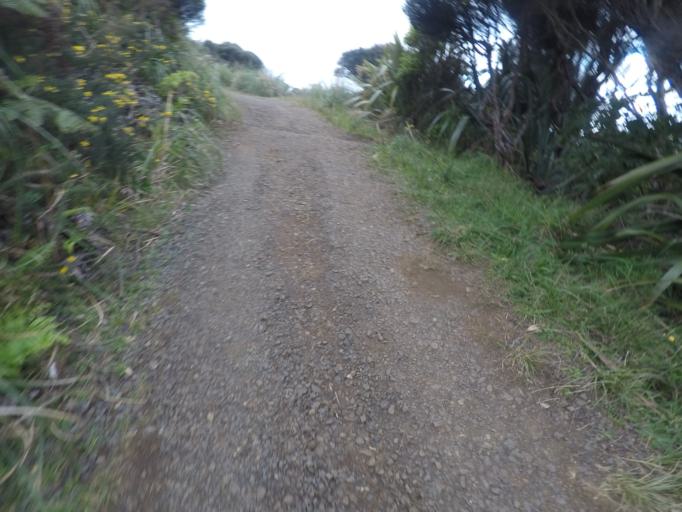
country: NZ
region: Auckland
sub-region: Auckland
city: Muriwai Beach
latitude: -36.9729
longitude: 174.4681
